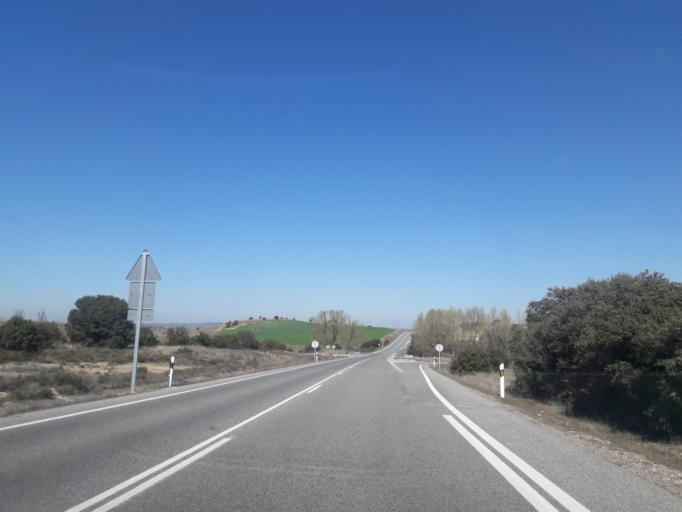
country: ES
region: Castille and Leon
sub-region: Provincia de Salamanca
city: Mozarbez
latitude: 40.8381
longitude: -5.6394
